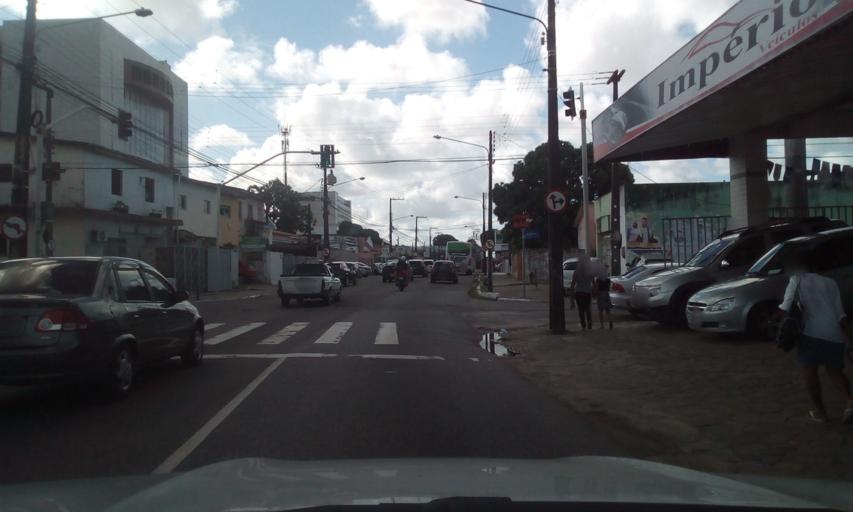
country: BR
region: Paraiba
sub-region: Joao Pessoa
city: Joao Pessoa
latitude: -7.1281
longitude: -34.8790
